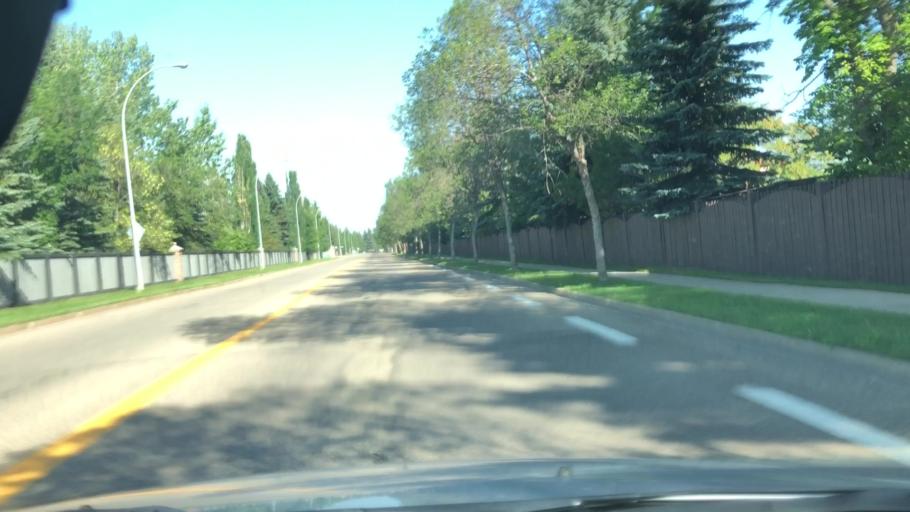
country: CA
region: Alberta
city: Edmonton
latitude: 53.4731
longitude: -113.5959
